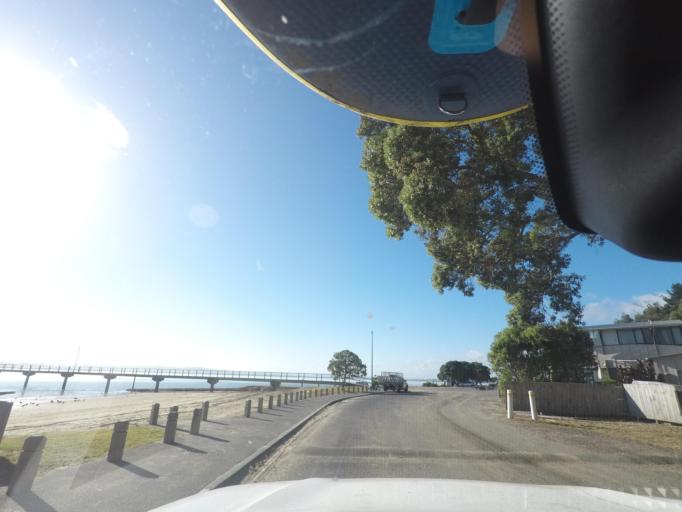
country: NZ
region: Auckland
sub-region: Auckland
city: Parakai
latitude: -36.5703
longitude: 174.3788
